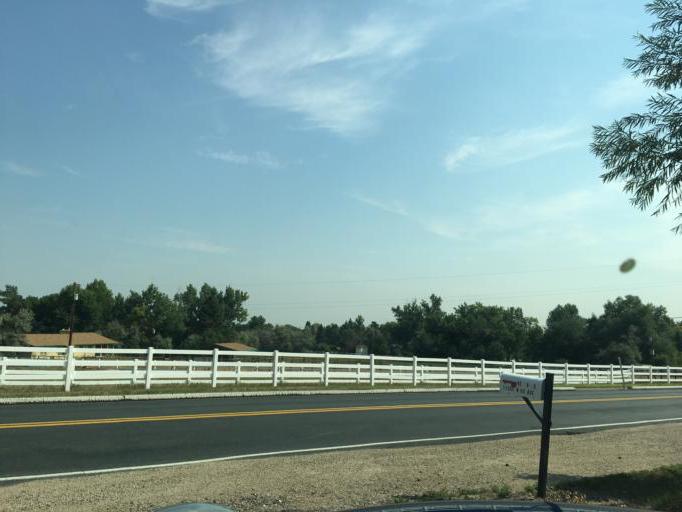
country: US
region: Colorado
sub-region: Jefferson County
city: Arvada
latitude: 39.8420
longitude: -105.1257
